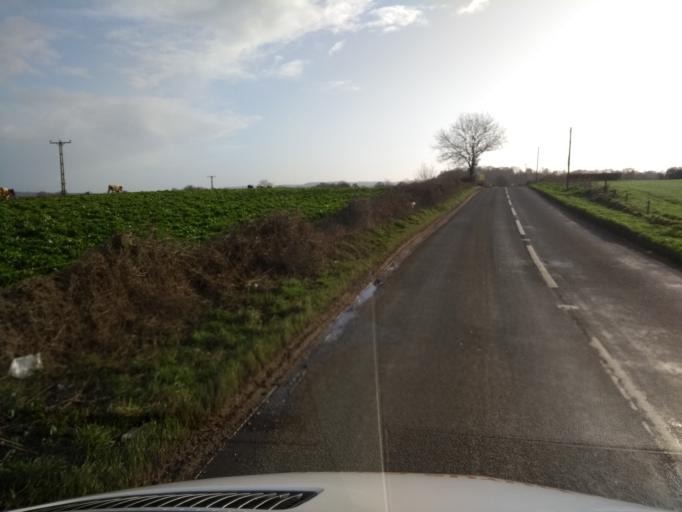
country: GB
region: England
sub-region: Somerset
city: Castle Cary
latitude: 51.0780
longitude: -2.5045
